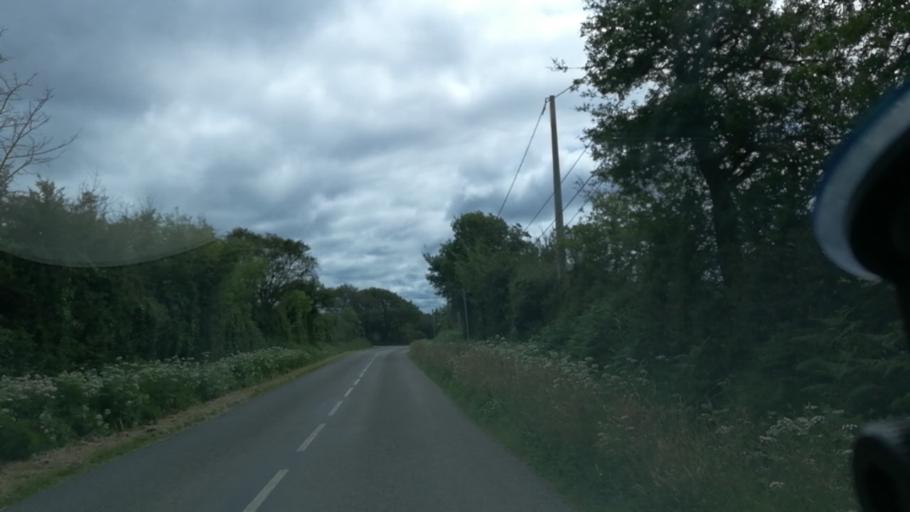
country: FR
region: Brittany
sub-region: Departement du Morbihan
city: Penestin
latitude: 47.4652
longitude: -2.4297
